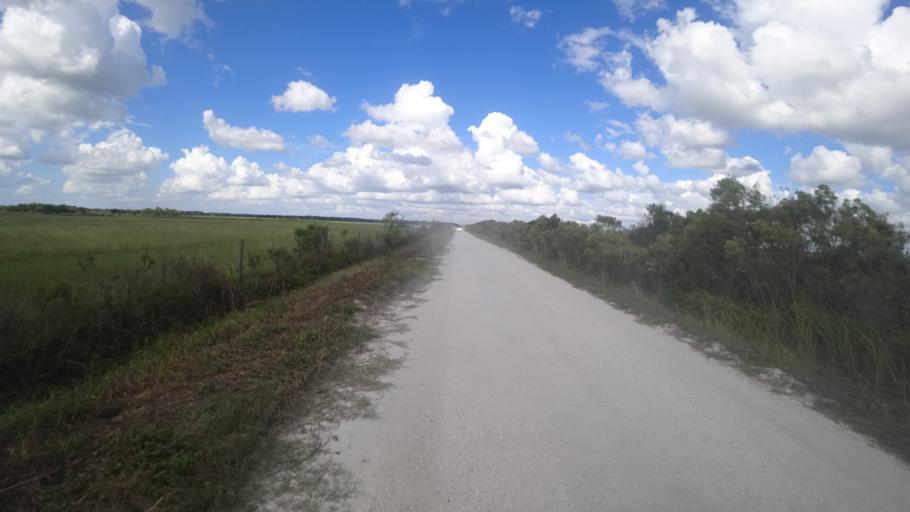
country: US
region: Florida
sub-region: DeSoto County
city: Arcadia
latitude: 27.3181
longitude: -82.1051
